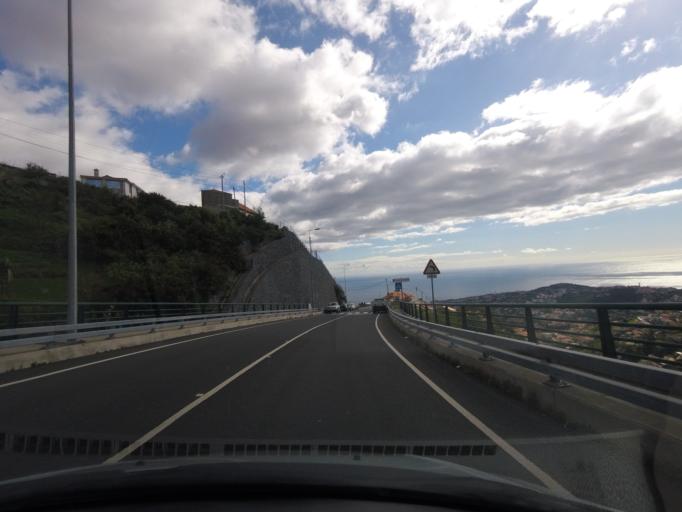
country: PT
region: Madeira
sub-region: Funchal
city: Nossa Senhora do Monte
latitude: 32.6782
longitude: -16.9409
